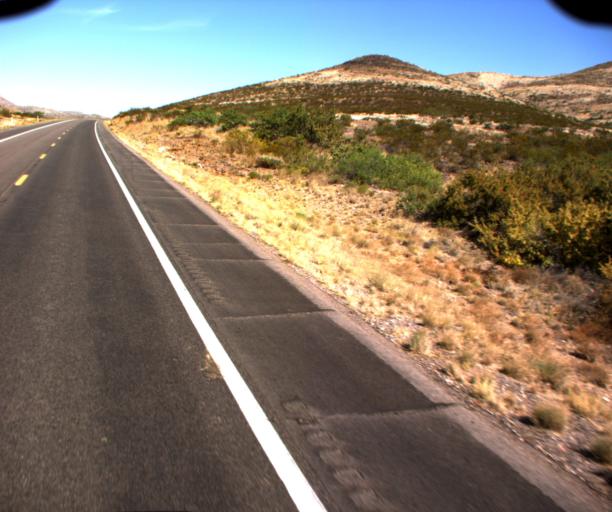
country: US
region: Arizona
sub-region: Greenlee County
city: Clifton
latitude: 32.7306
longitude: -109.1863
